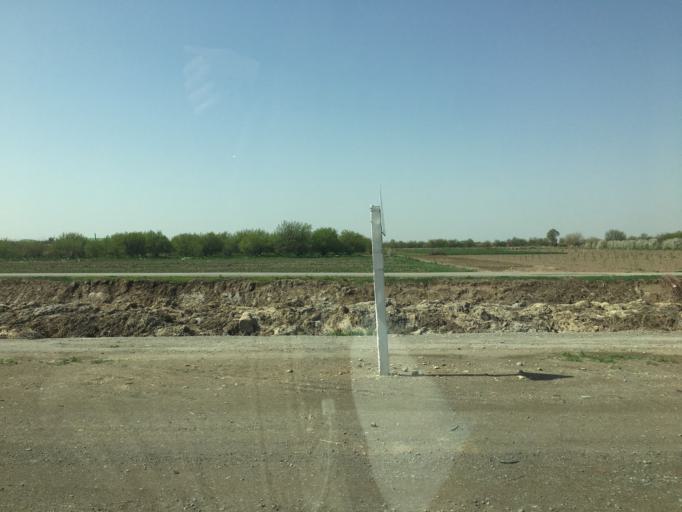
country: TM
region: Lebap
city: Turkmenabat
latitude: 38.9695
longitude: 63.6538
